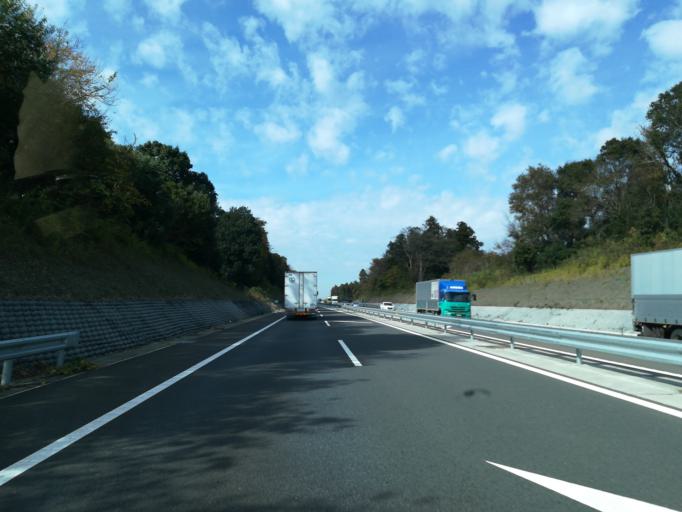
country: JP
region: Ibaraki
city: Mitsukaido
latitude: 36.0656
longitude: 140.0275
